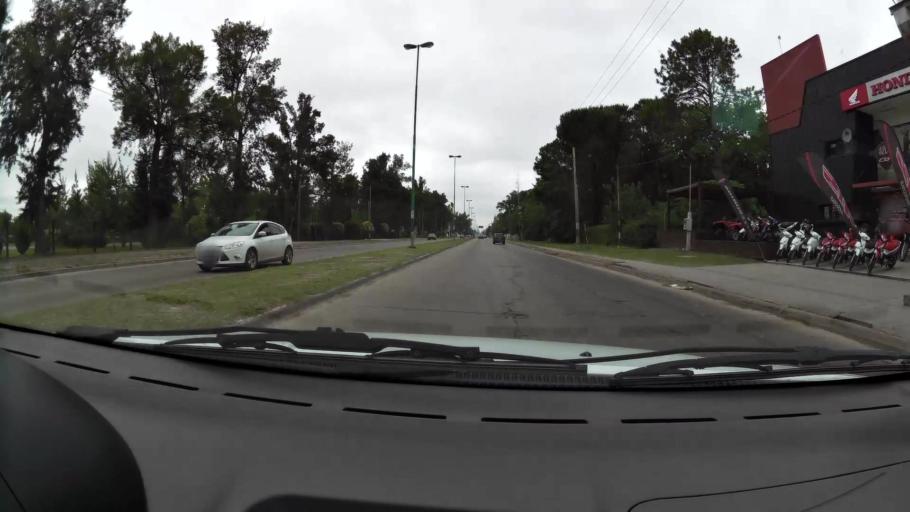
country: AR
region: Buenos Aires
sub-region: Partido de La Plata
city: La Plata
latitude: -34.9588
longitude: -58.0080
